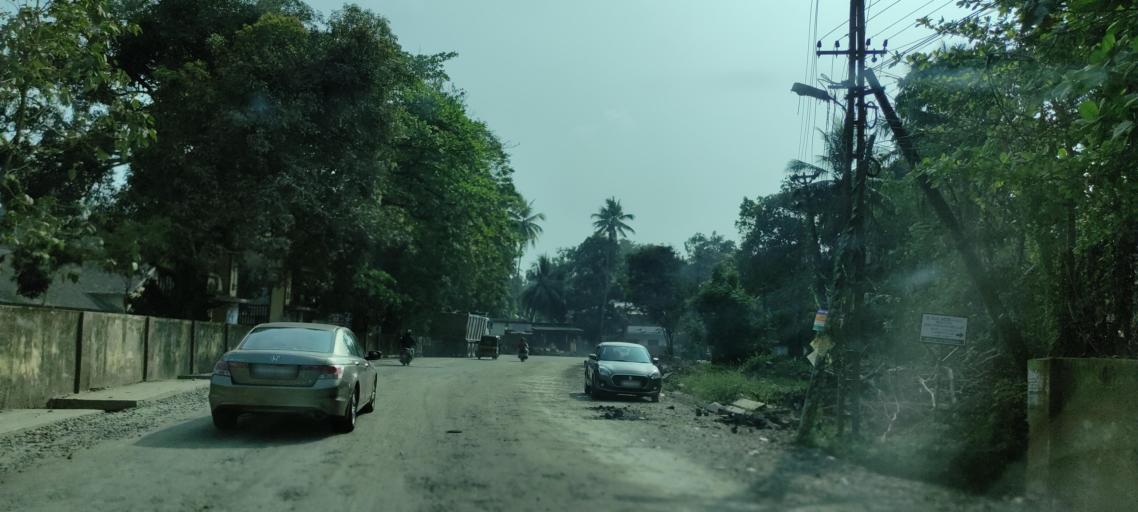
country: IN
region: Kerala
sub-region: Pattanamtitta
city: Tiruvalla
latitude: 9.3759
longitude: 76.5554
